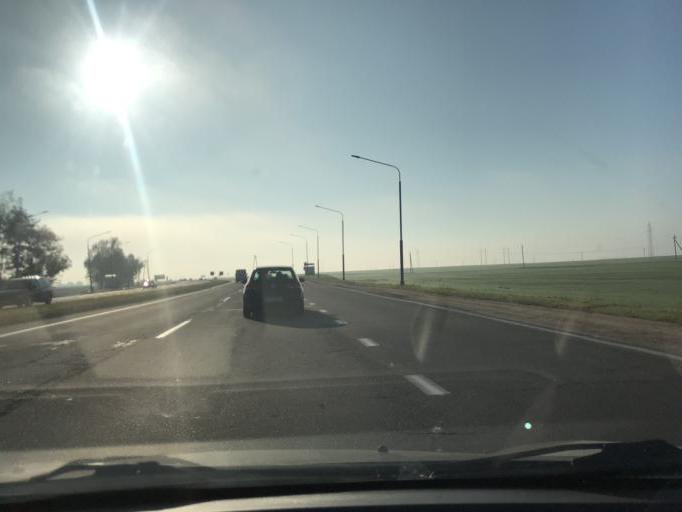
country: BY
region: Minsk
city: Dukora
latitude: 53.7050
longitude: 27.8784
